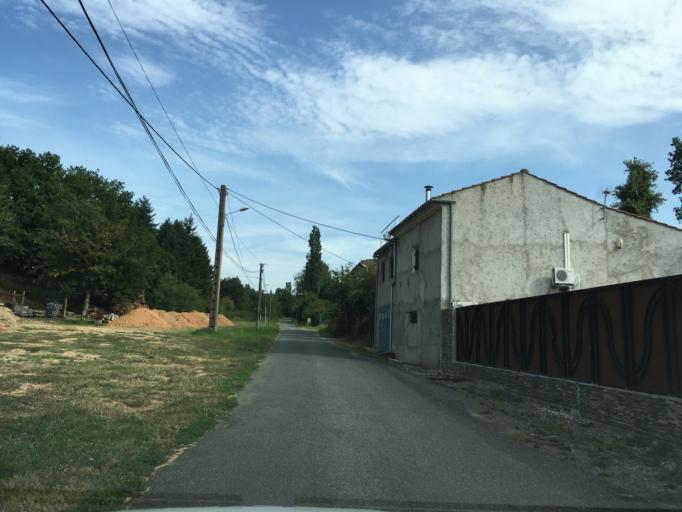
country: FR
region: Midi-Pyrenees
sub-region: Departement du Tarn
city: Castres
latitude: 43.6068
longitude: 2.2772
